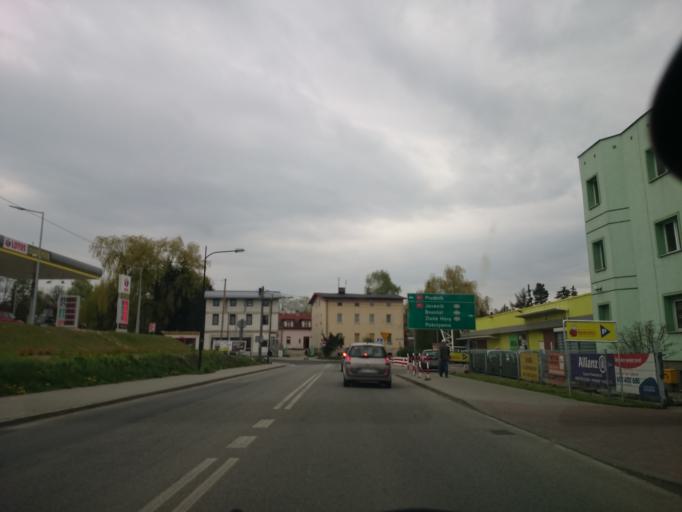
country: PL
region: Opole Voivodeship
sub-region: Powiat nyski
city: Glucholazy
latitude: 50.3176
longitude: 17.3882
